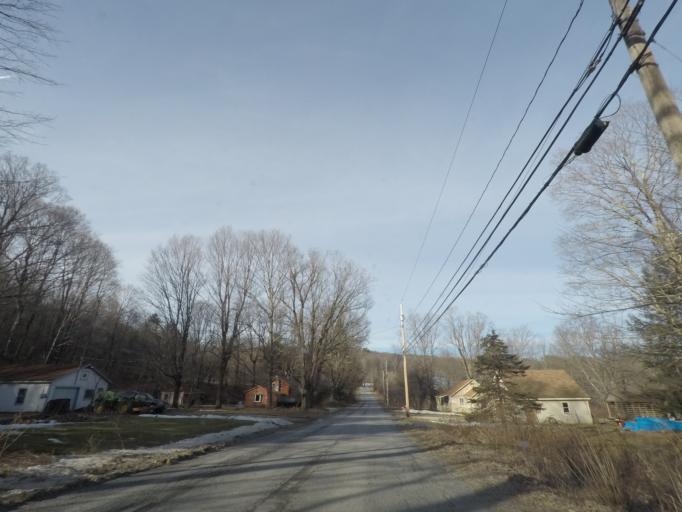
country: US
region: Massachusetts
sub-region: Berkshire County
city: Williamstown
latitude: 42.7371
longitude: -73.3625
